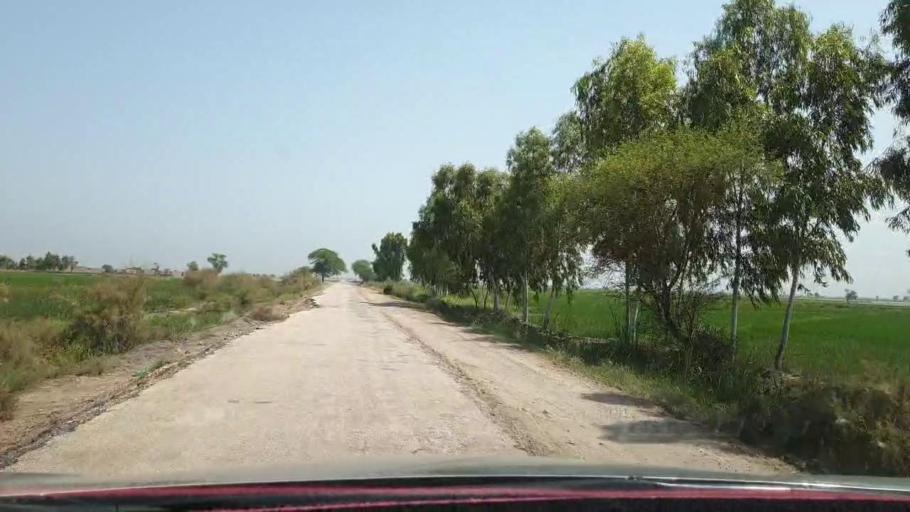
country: PK
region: Sindh
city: Warah
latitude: 27.3815
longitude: 67.7858
